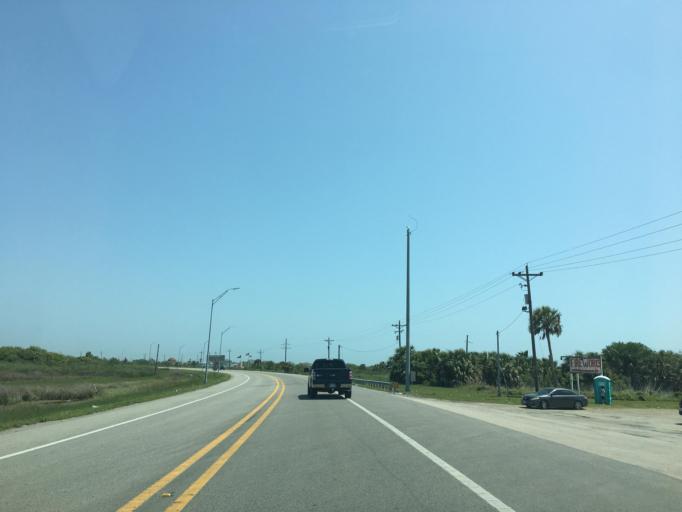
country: US
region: Texas
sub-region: Galveston County
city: Galveston
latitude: 29.3668
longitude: -94.7620
